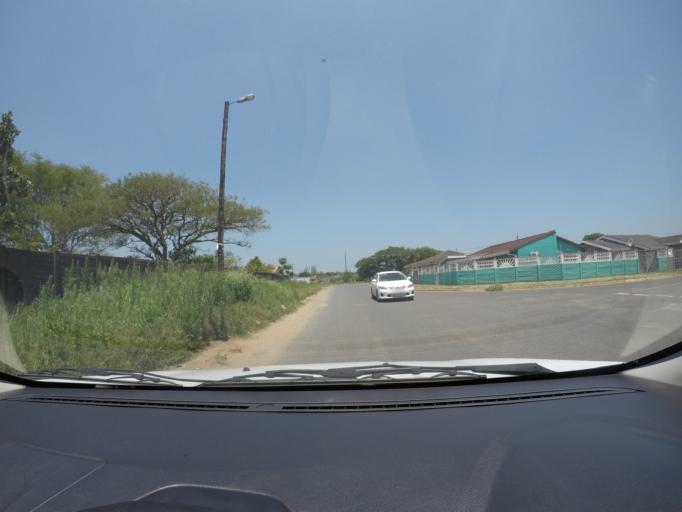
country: ZA
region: KwaZulu-Natal
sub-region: uThungulu District Municipality
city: eSikhawini
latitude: -28.8874
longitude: 31.8905
